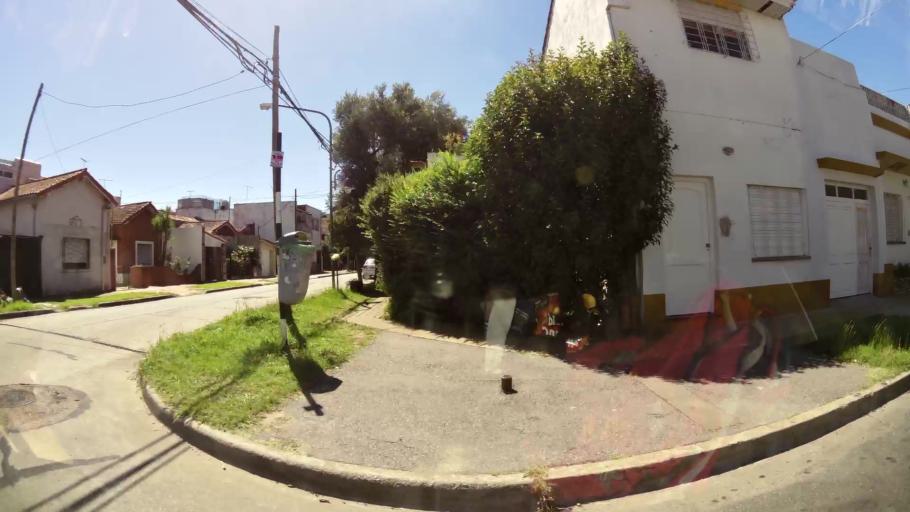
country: AR
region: Buenos Aires
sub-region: Partido de General San Martin
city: General San Martin
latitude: -34.5276
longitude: -58.5331
